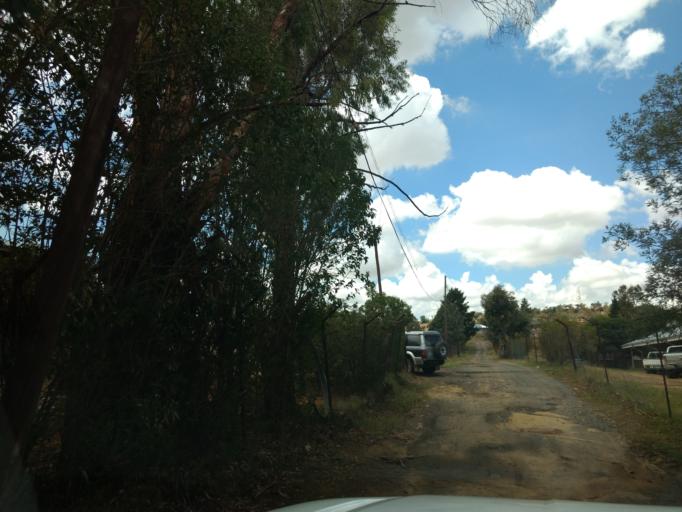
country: LS
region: Maseru
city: Maseru
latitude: -29.3961
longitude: 27.5533
